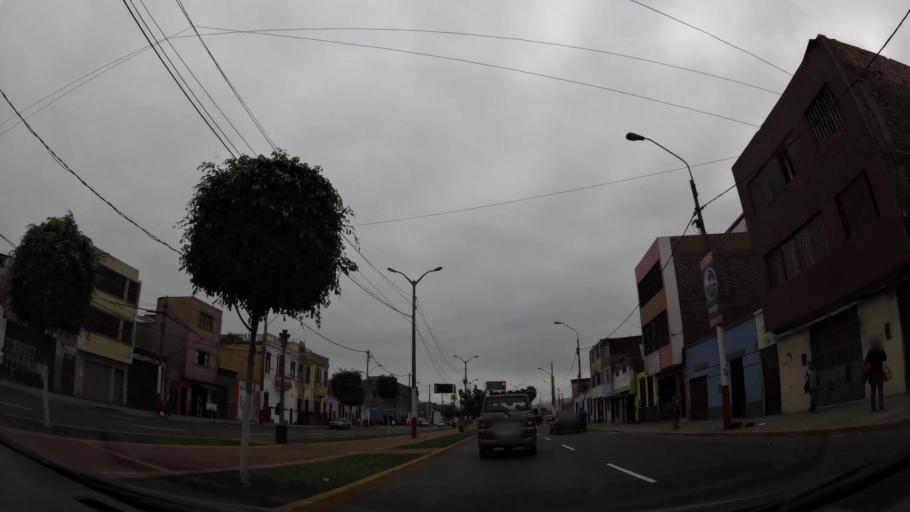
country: PE
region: Callao
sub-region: Callao
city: Callao
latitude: -12.0627
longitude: -77.1405
